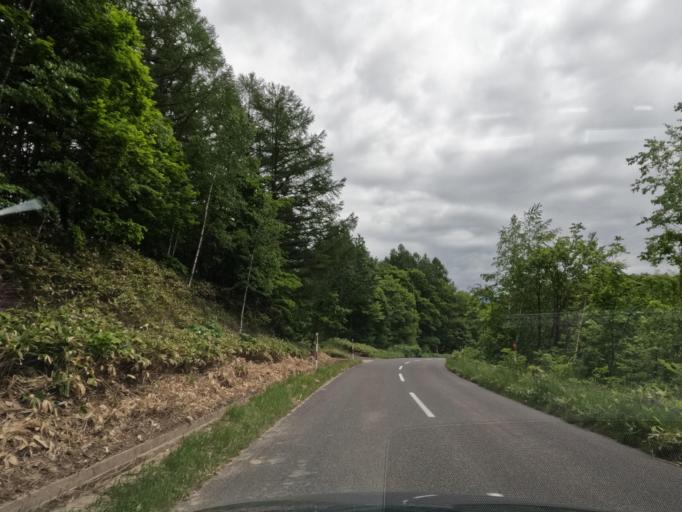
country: JP
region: Hokkaido
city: Shimo-furano
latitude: 43.4949
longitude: 142.4185
